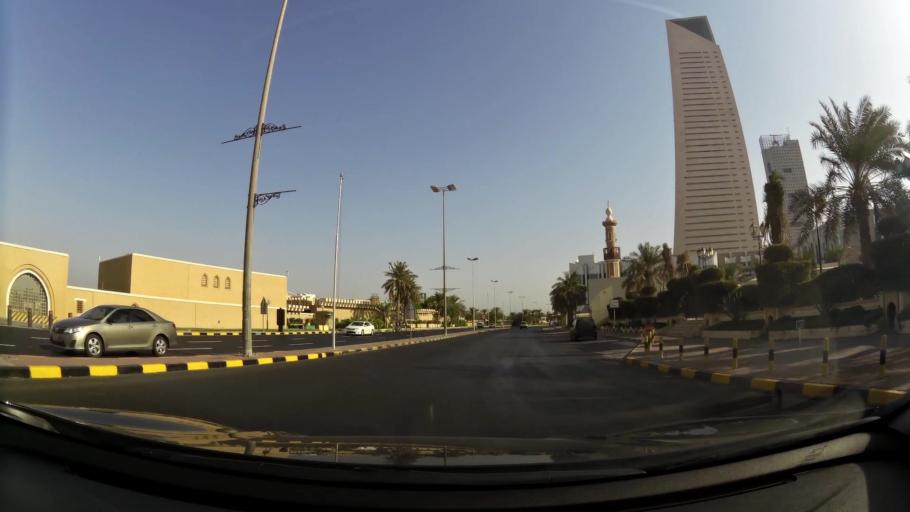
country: KW
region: Al Asimah
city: Kuwait City
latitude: 29.3804
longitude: 47.9740
